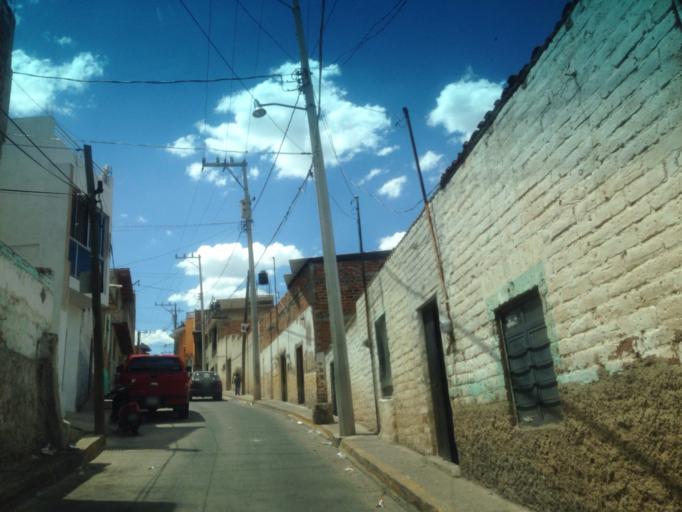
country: MX
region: Jalisco
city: Atotonilco el Alto
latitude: 20.5549
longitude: -102.5105
